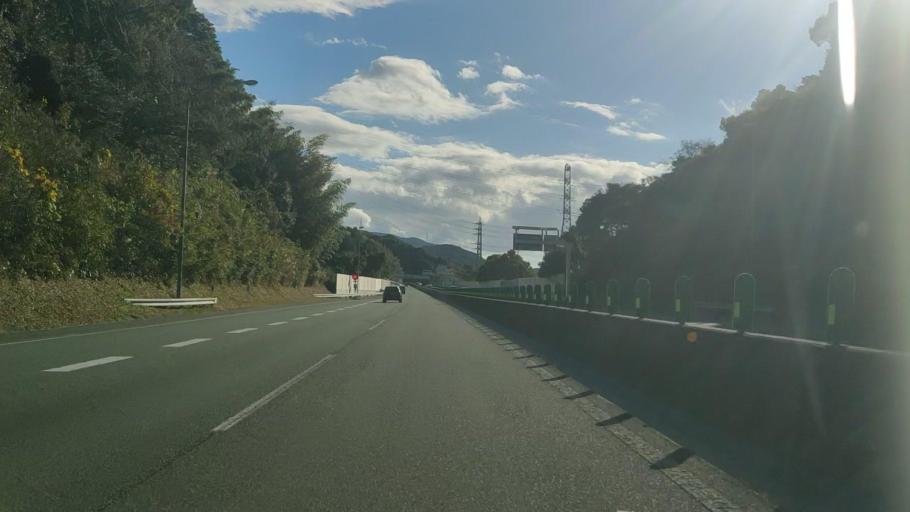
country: JP
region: Fukuoka
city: Kitakyushu
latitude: 33.8387
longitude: 130.7654
